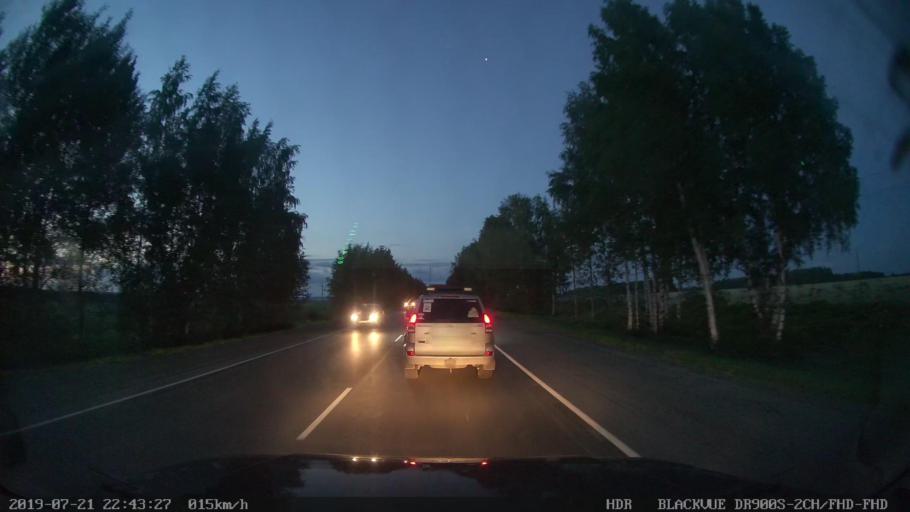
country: RU
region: Perm
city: Ust'-Kachka
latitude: 58.0521
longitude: 55.5959
